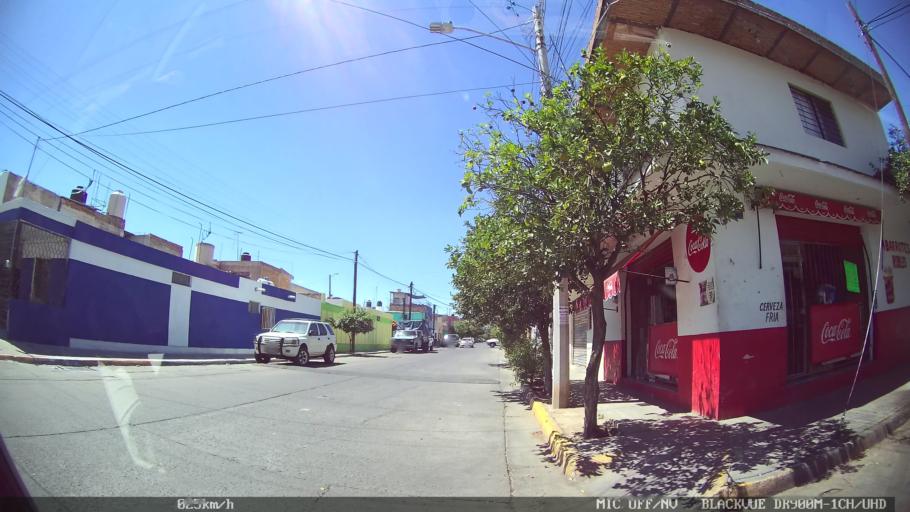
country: MX
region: Jalisco
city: Tlaquepaque
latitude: 20.6695
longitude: -103.2900
